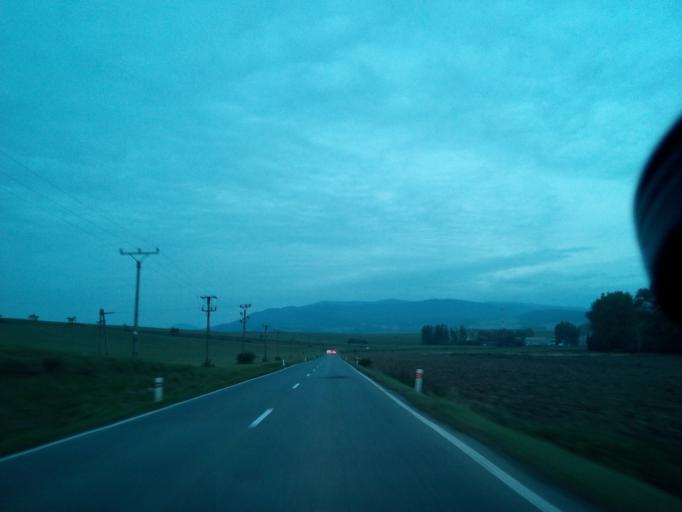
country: SK
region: Presovsky
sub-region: Okres Presov
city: Presov
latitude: 49.0642
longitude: 21.3416
